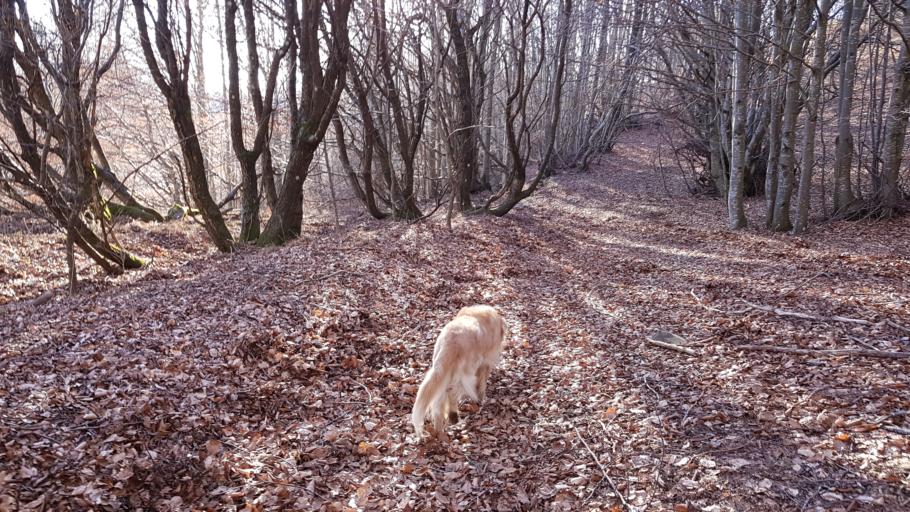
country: IT
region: Liguria
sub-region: Provincia di Genova
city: Torriglia
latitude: 44.5482
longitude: 9.1527
